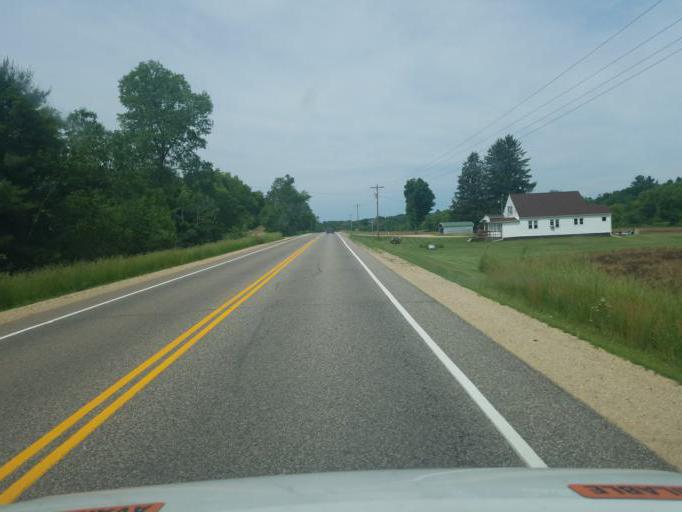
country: US
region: Wisconsin
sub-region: Juneau County
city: Elroy
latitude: 43.7656
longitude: -90.2430
